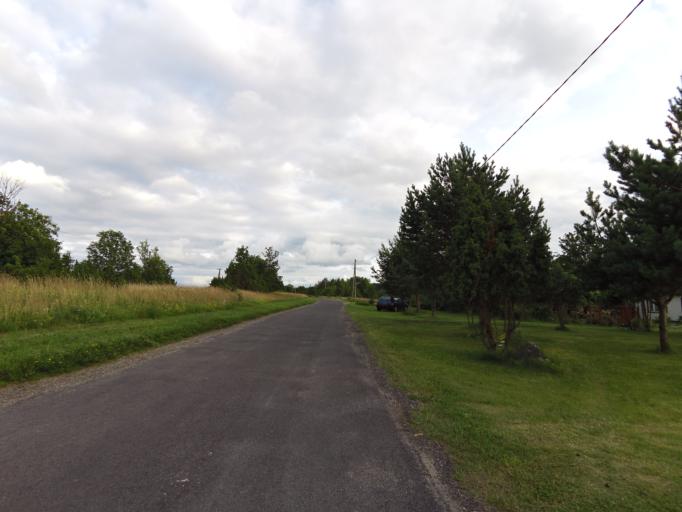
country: EE
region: Laeaene
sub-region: Vormsi vald
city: Hullo
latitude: 58.9872
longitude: 23.2459
